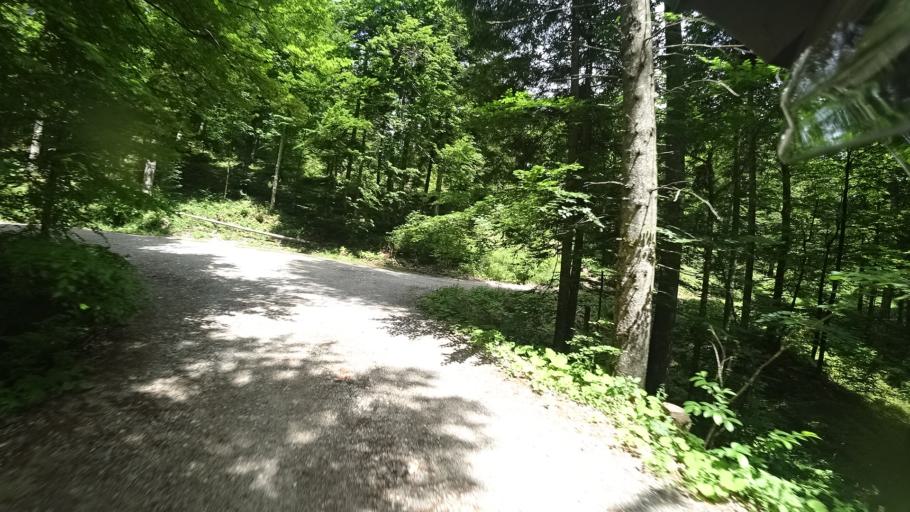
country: SI
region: Osilnica
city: Osilnica
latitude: 45.5160
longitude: 14.6130
